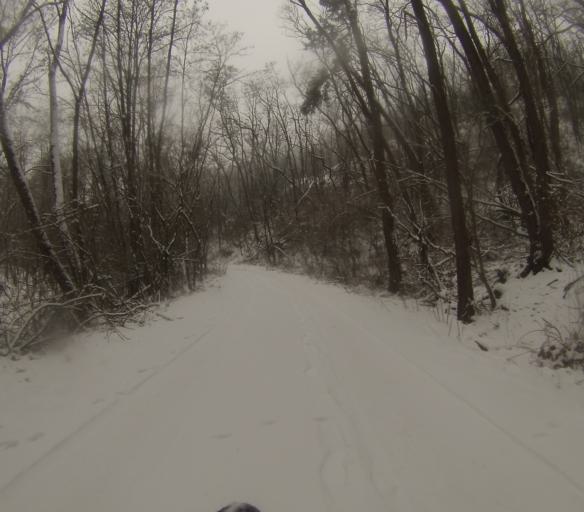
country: CZ
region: South Moravian
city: Orechov
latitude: 49.1343
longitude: 16.5335
